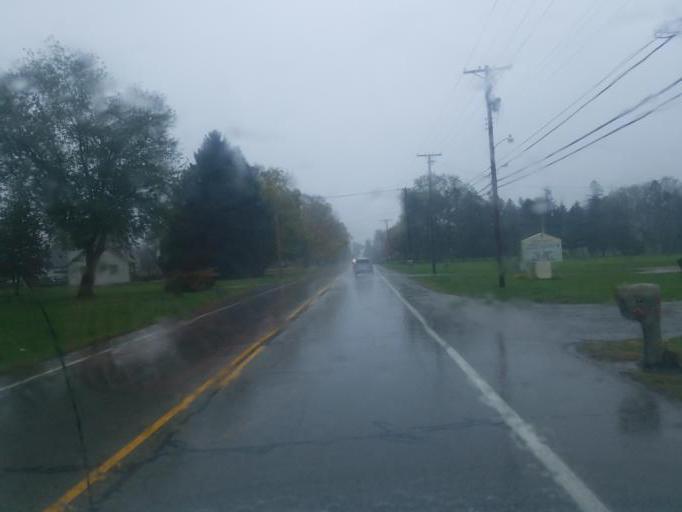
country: US
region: Ohio
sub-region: Muskingum County
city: Zanesville
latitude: 39.9636
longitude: -82.0436
